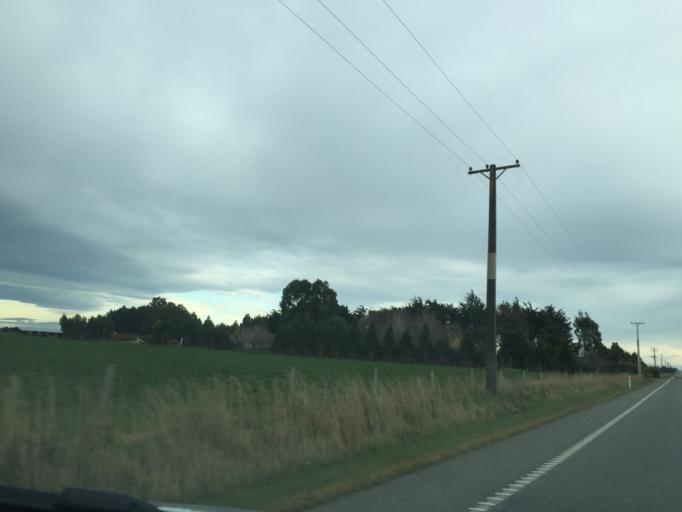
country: NZ
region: Southland
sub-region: Gore District
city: Gore
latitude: -46.3096
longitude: 168.7048
